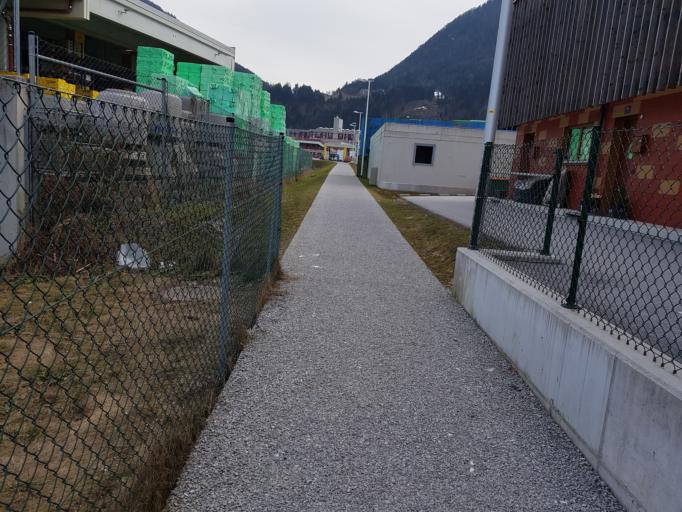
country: AT
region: Tyrol
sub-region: Politischer Bezirk Kufstein
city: Worgl
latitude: 47.4833
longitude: 12.0571
